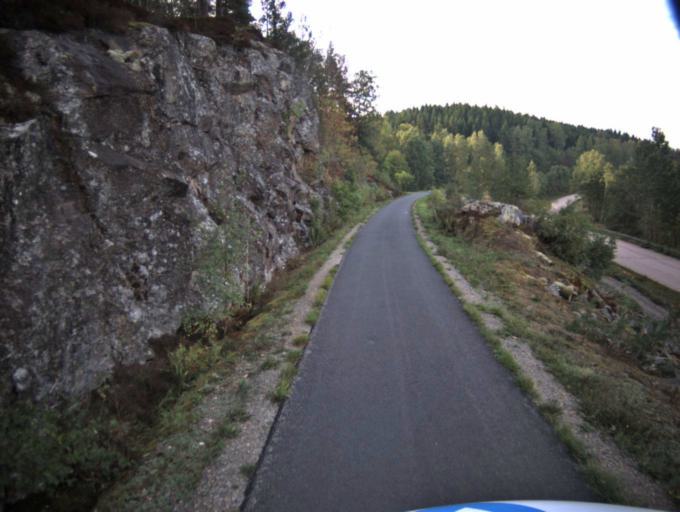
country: SE
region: Vaestra Goetaland
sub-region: Ulricehamns Kommun
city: Ulricehamn
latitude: 57.7590
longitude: 13.3999
